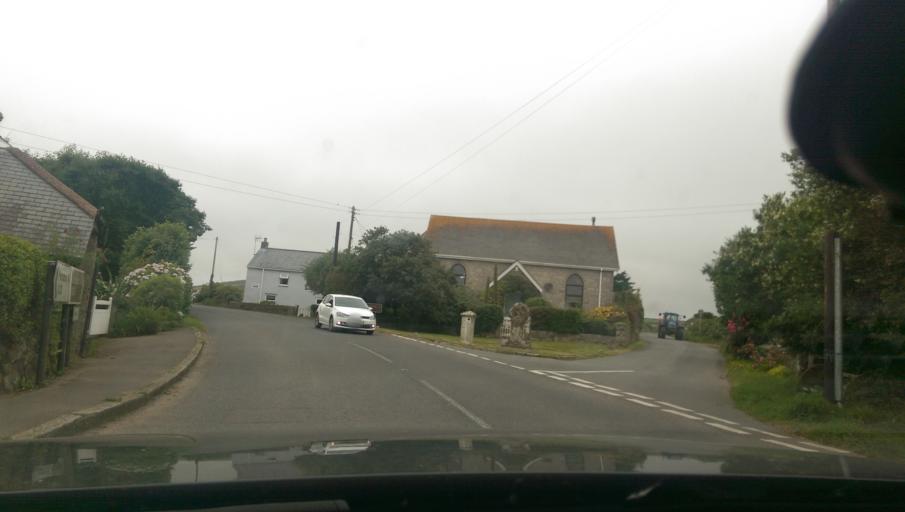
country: GB
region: England
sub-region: Cornwall
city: St. Buryan
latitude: 50.0913
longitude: -5.6426
